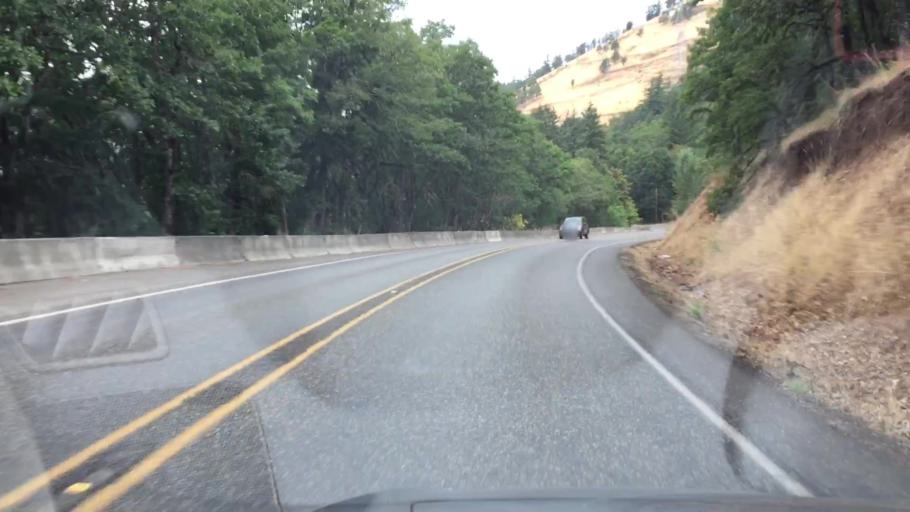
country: US
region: Washington
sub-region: Klickitat County
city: White Salmon
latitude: 45.7537
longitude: -121.5168
